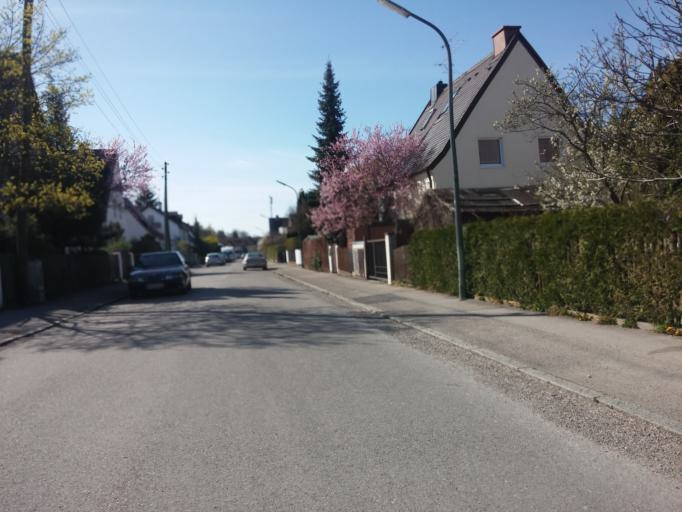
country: DE
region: Bavaria
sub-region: Upper Bavaria
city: Neubiberg
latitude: 48.0825
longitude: 11.6704
